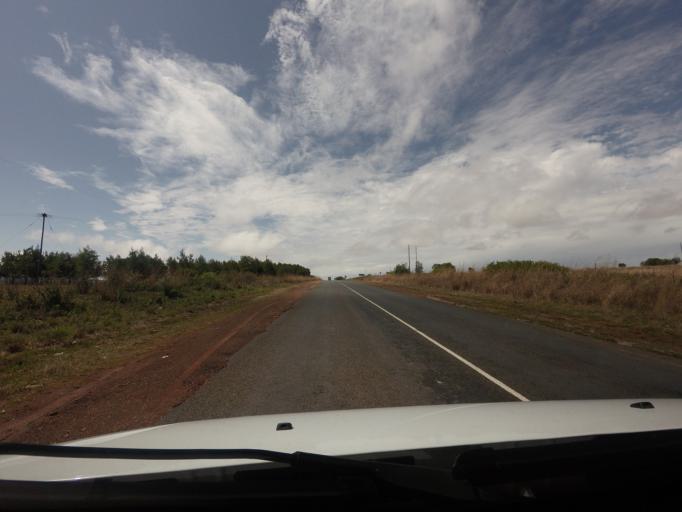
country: ZA
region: Mpumalanga
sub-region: Ehlanzeni District
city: Lydenburg
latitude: -25.1693
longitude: 30.3736
